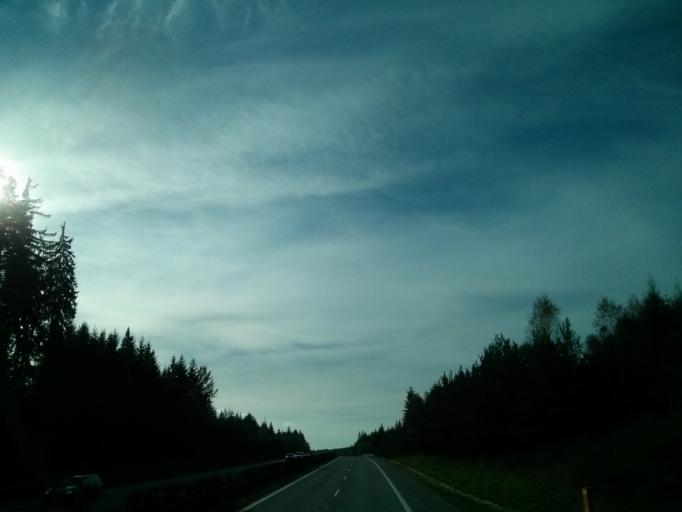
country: CZ
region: Plzensky
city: Holoubkov
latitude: 49.7812
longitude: 13.6885
